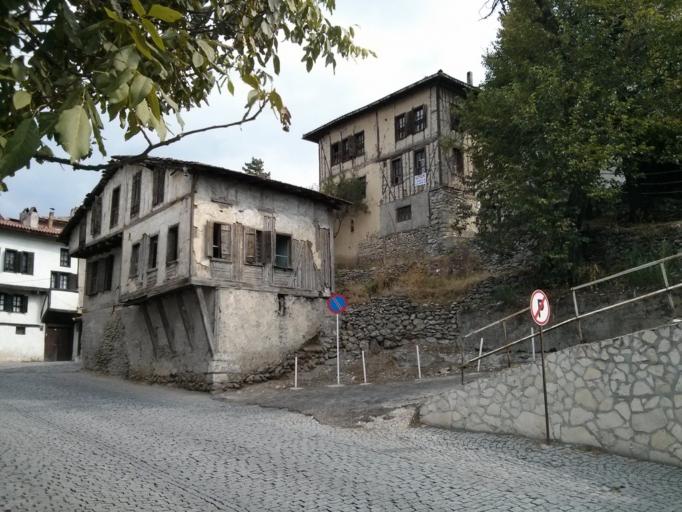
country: TR
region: Karabuk
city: Safranbolu
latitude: 41.2468
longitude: 32.6935
